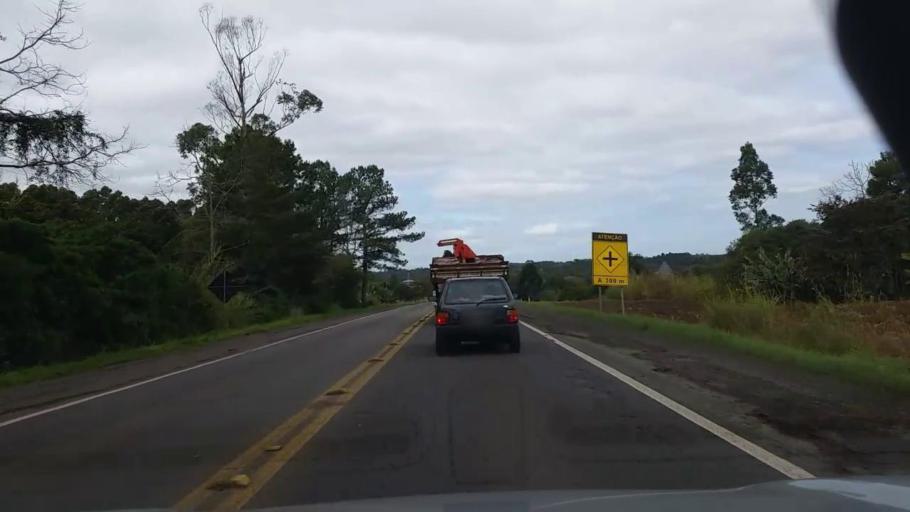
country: BR
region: Rio Grande do Sul
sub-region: Arroio Do Meio
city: Arroio do Meio
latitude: -29.4026
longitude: -52.0385
